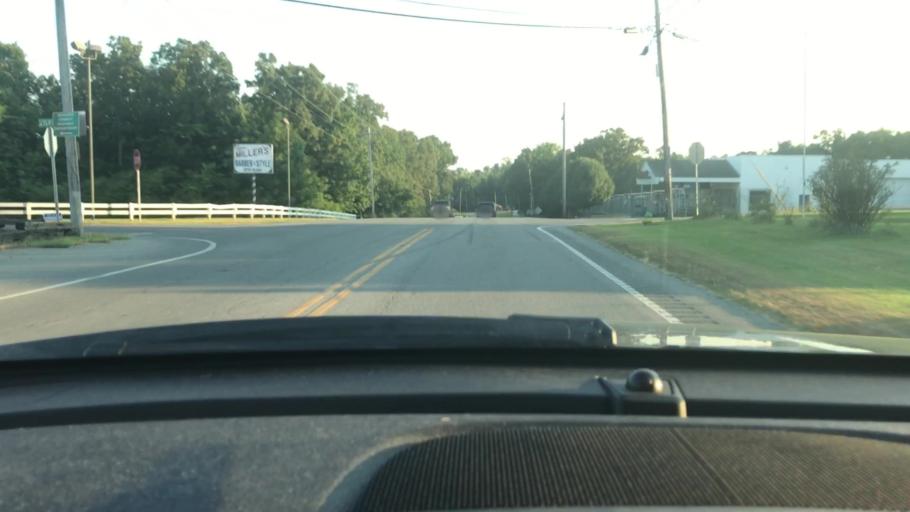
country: US
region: Tennessee
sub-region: Dickson County
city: Dickson
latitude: 36.1078
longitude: -87.3721
